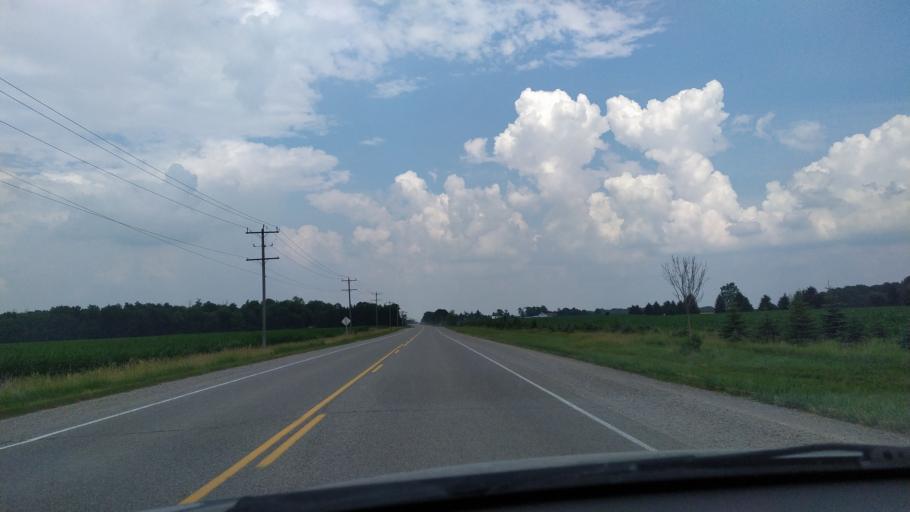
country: CA
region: Ontario
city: London
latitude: 43.1531
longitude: -81.1815
